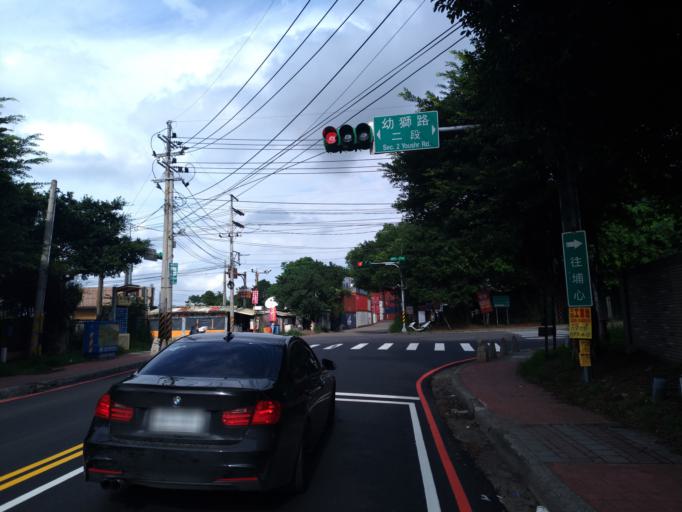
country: TW
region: Taiwan
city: Daxi
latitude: 24.9298
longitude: 121.1727
